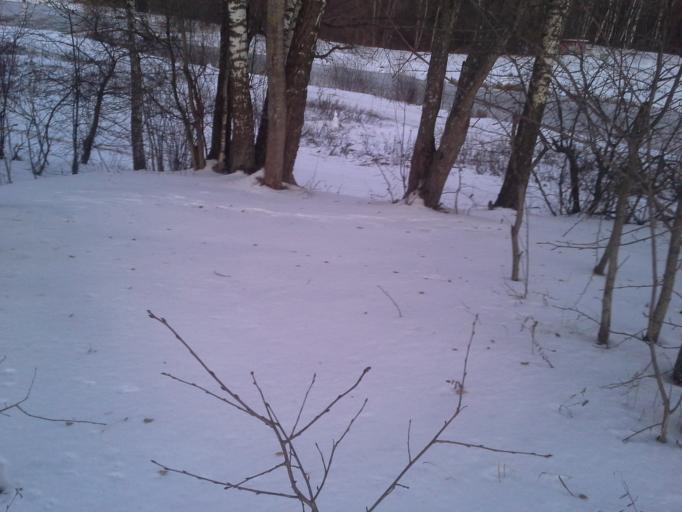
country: RU
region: Moscow
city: Yasenevo
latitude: 55.5832
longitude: 37.5430
